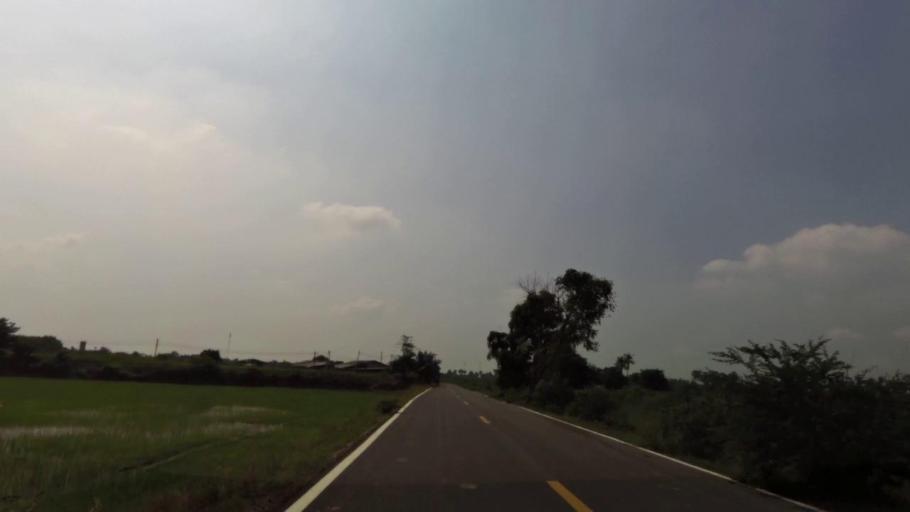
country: TH
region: Ang Thong
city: Pho Thong
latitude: 14.6134
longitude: 100.3989
